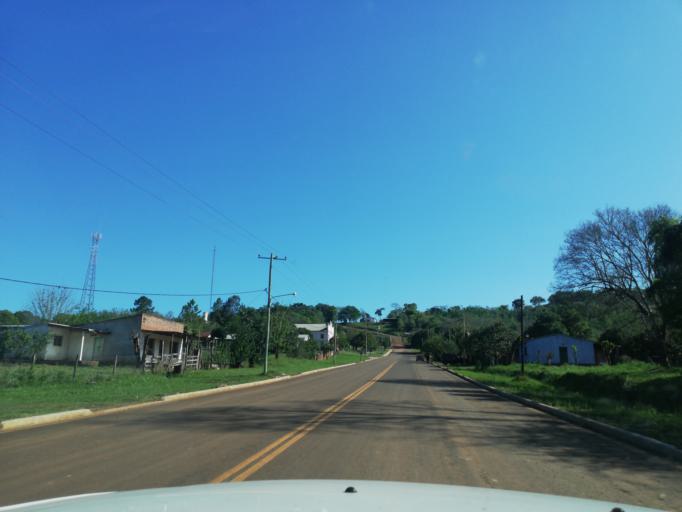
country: AR
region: Misiones
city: Arroyo del Medio
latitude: -27.6961
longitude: -55.4038
